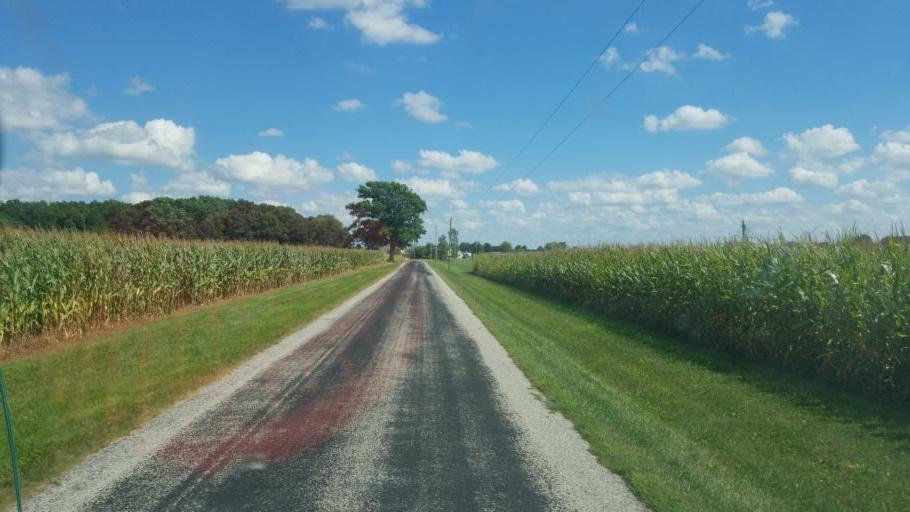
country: US
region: Ohio
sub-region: Marion County
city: Prospect
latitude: 40.3631
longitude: -83.2098
